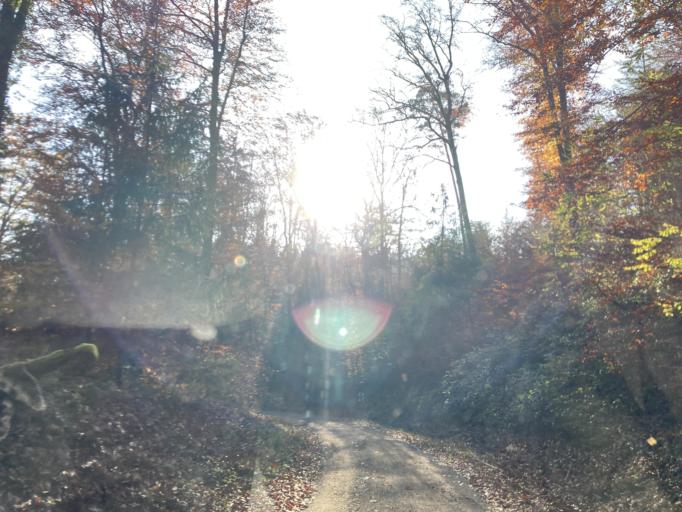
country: DE
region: Baden-Wuerttemberg
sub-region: Tuebingen Region
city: Tuebingen
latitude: 48.5467
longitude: 8.9931
